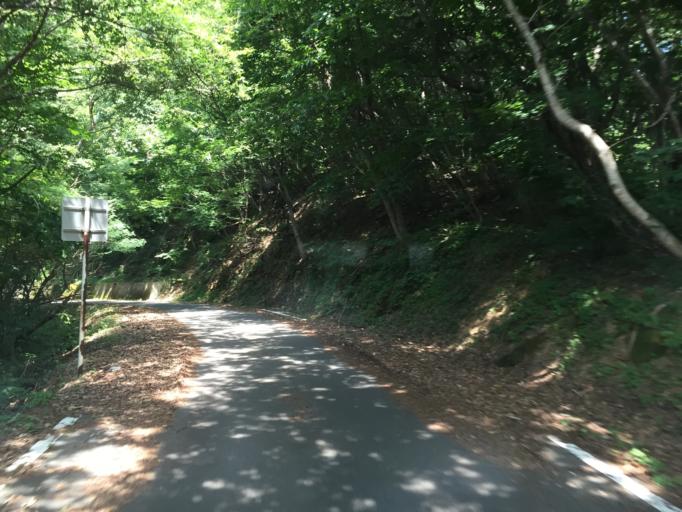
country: JP
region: Fukushima
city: Inawashiro
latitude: 37.4403
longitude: 140.0612
